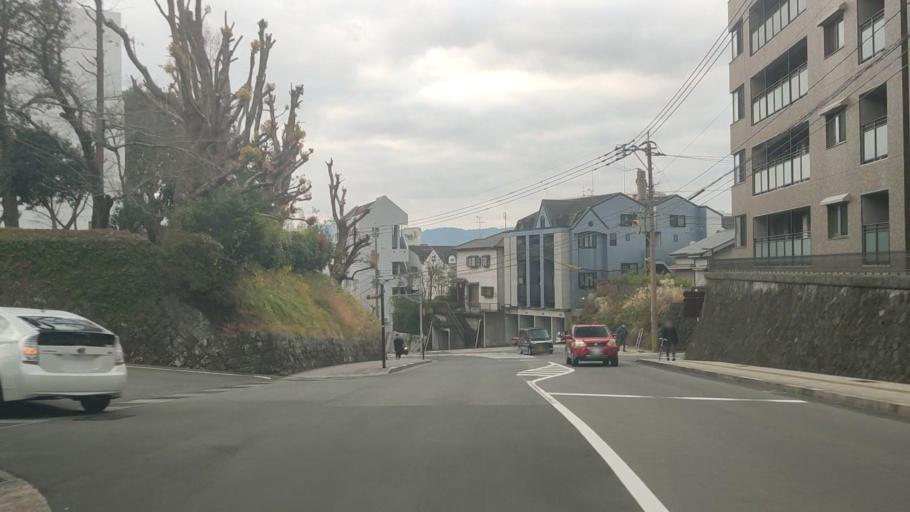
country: JP
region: Nagasaki
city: Nagasaki-shi
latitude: 32.7722
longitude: 129.8672
